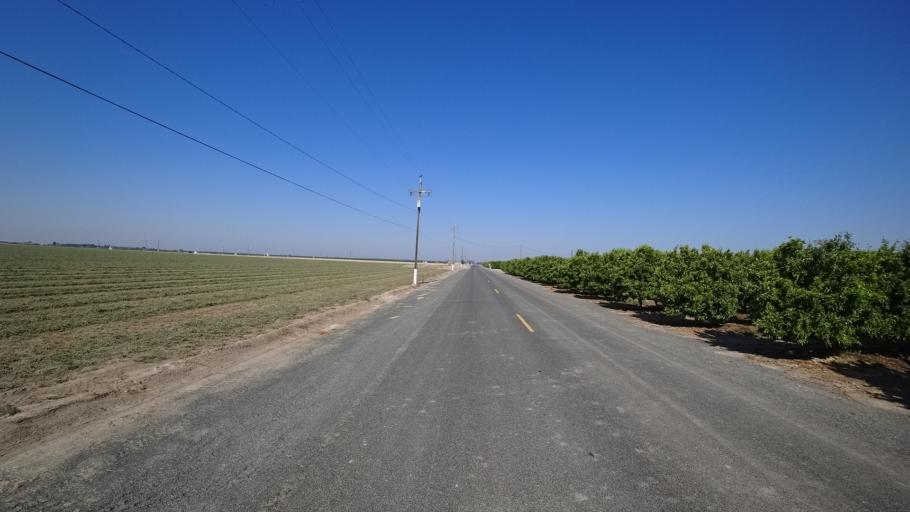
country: US
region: California
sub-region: Kings County
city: Hanford
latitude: 36.3866
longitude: -119.5613
